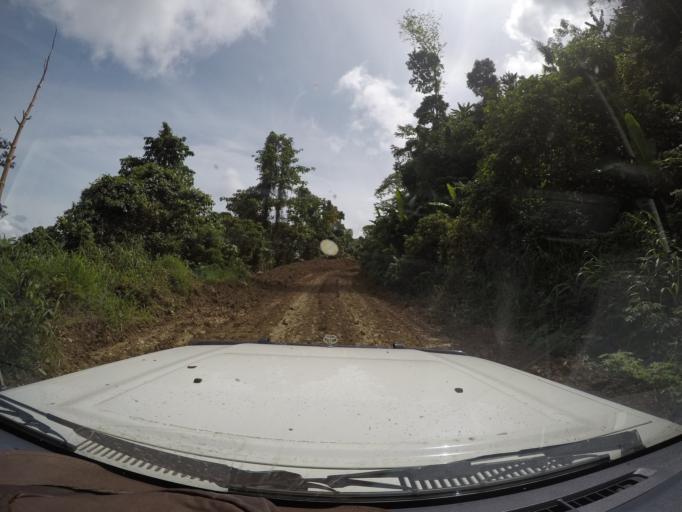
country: PG
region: Gulf
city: Kerema
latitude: -7.9924
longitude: 145.8311
